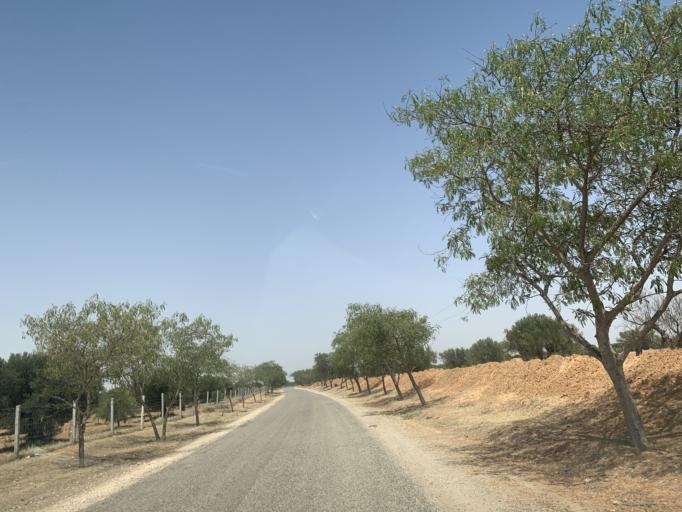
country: TN
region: Al Mahdiyah
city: Shurban
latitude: 35.1909
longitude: 10.2484
